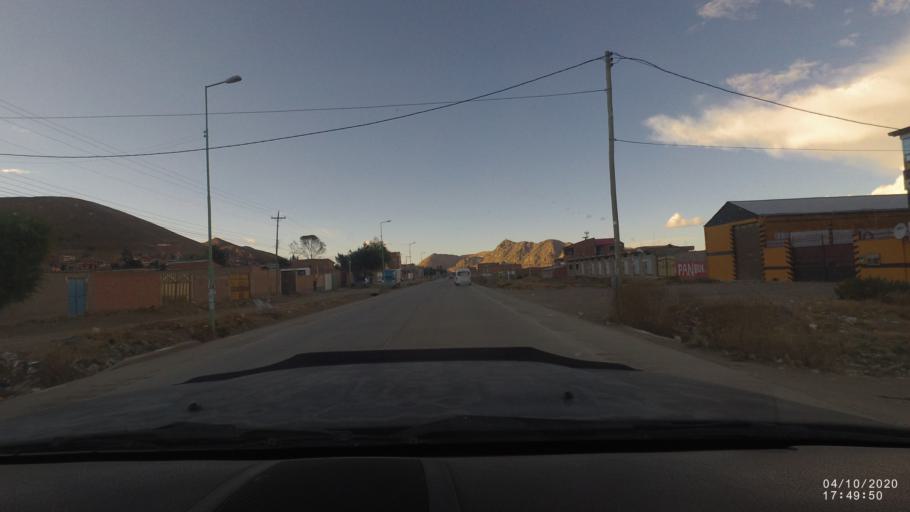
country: BO
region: Oruro
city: Oruro
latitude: -18.0065
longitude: -67.1360
